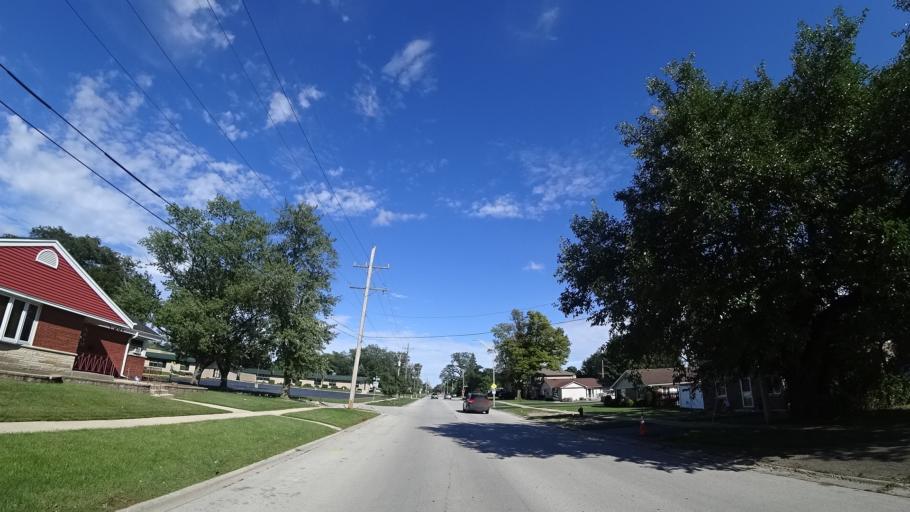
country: US
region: Illinois
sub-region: Cook County
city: Oak Lawn
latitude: 41.7127
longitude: -87.7467
